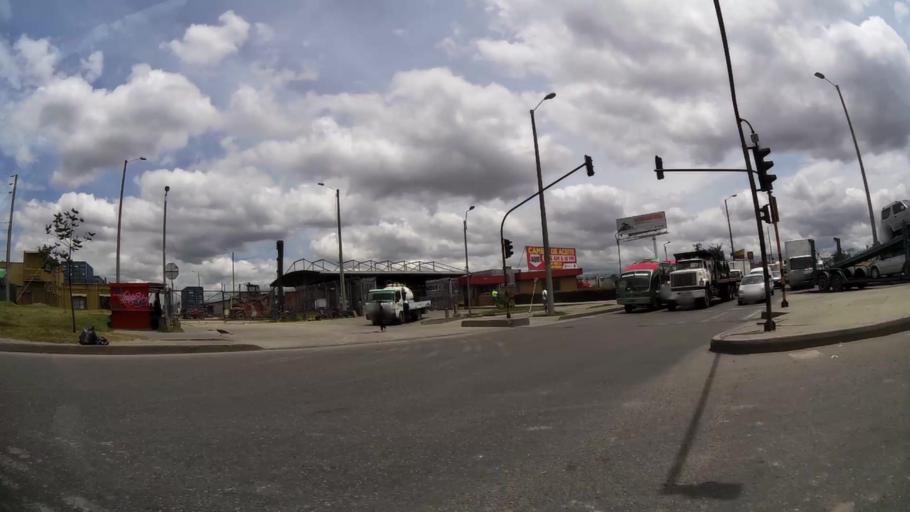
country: CO
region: Bogota D.C.
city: Bogota
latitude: 4.6552
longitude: -74.1407
